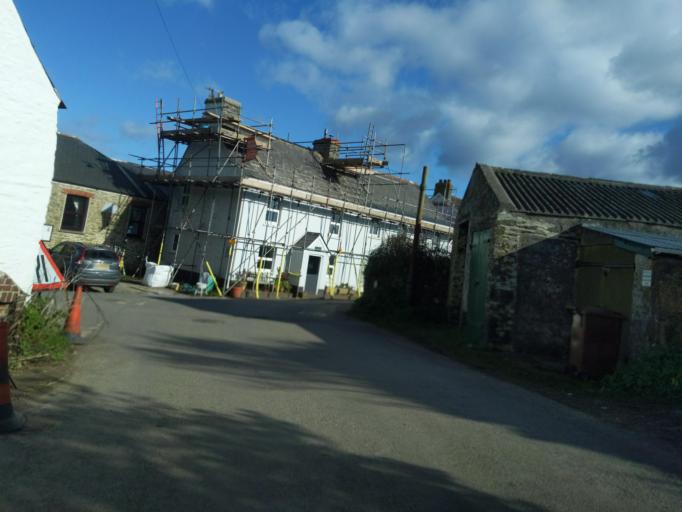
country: GB
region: England
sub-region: Devon
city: Salcombe
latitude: 50.2153
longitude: -3.7110
